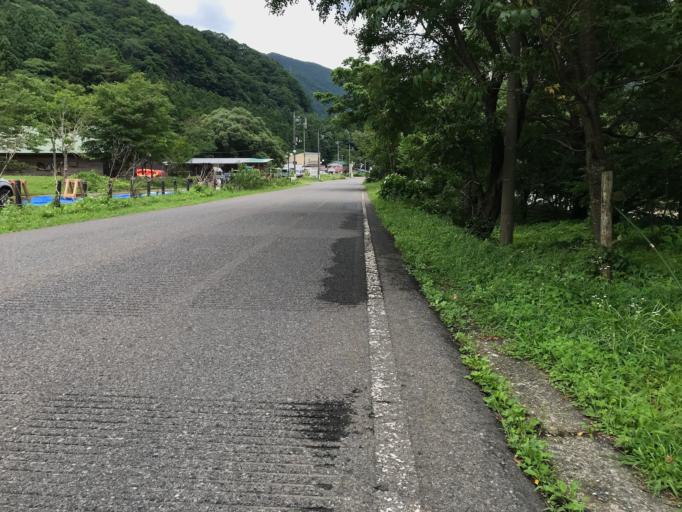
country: JP
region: Gunma
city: Numata
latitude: 36.8130
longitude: 138.9856
